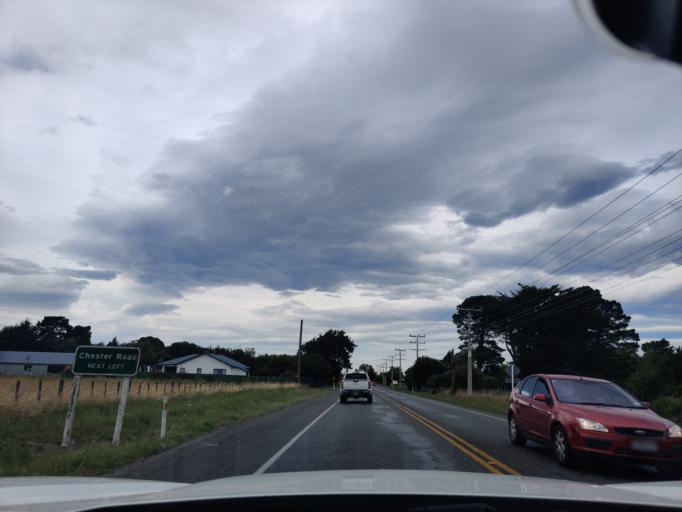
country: NZ
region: Wellington
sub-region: Masterton District
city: Masterton
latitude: -41.0095
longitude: 175.5486
